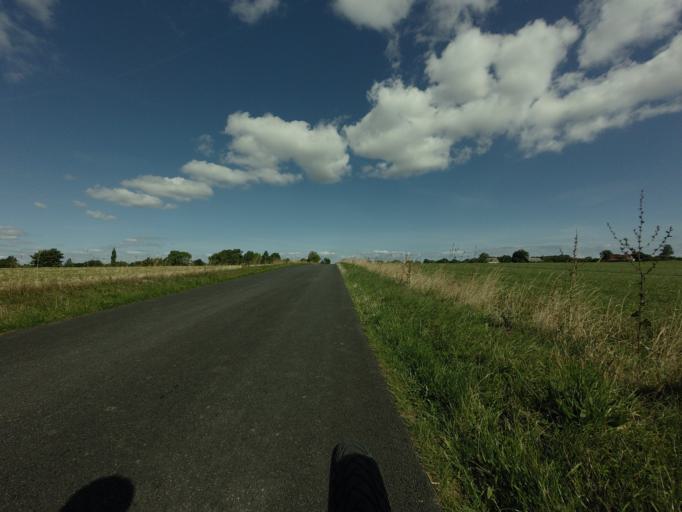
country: DK
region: Zealand
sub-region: Vordingborg Kommune
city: Stege
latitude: 54.9714
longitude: 12.3590
